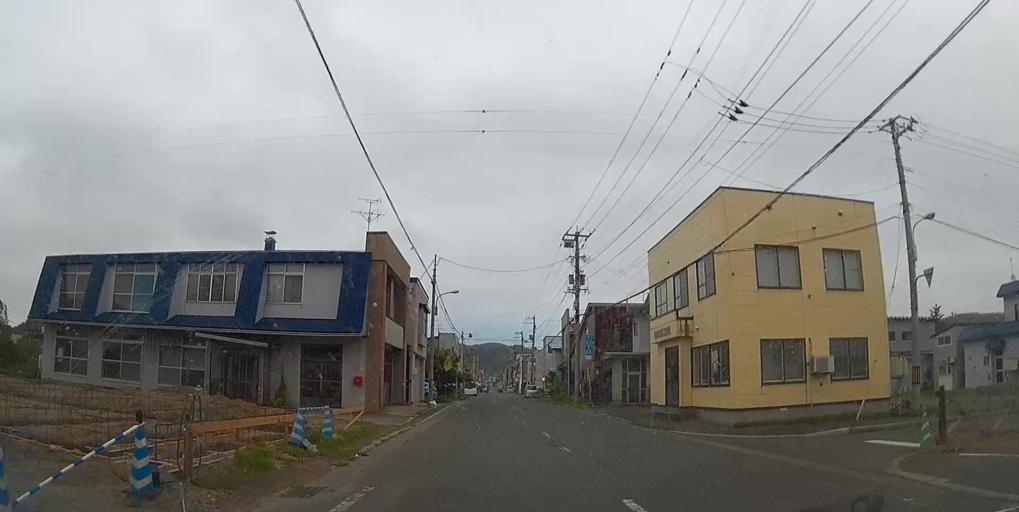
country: JP
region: Hokkaido
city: Iwanai
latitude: 42.4255
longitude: 140.0108
